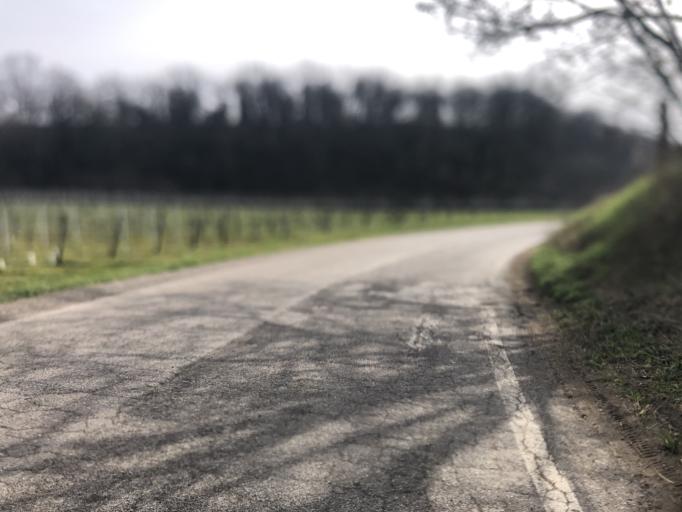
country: IT
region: Veneto
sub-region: Provincia di Verona
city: San Giorgio in Salici
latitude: 45.4108
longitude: 10.7746
